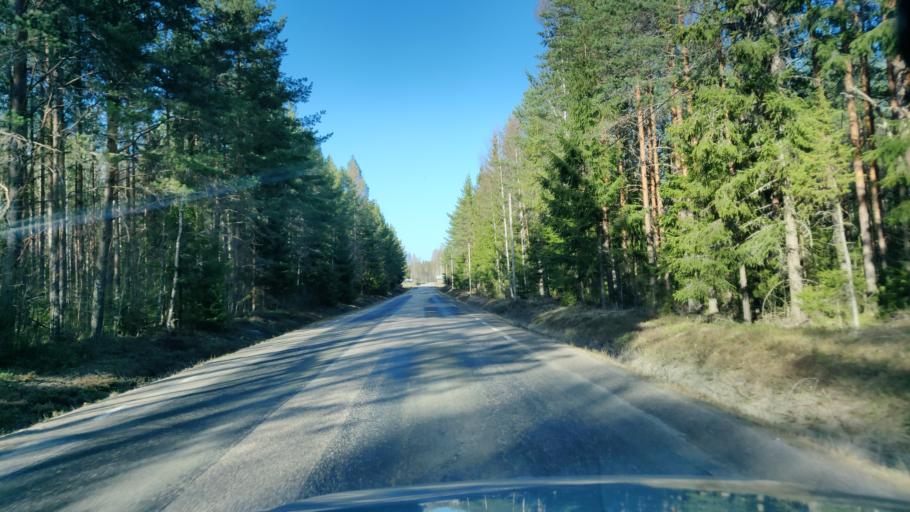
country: SE
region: Vaermland
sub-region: Sunne Kommun
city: Sunne
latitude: 59.9820
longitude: 13.2589
